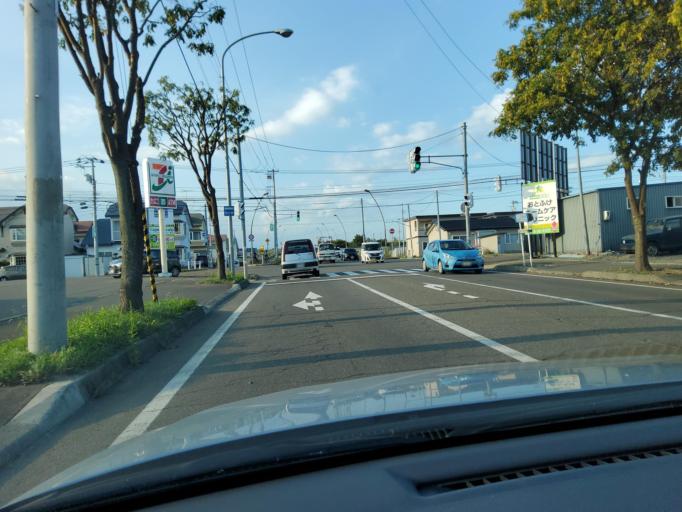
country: JP
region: Hokkaido
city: Obihiro
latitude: 42.9402
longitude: 143.1838
